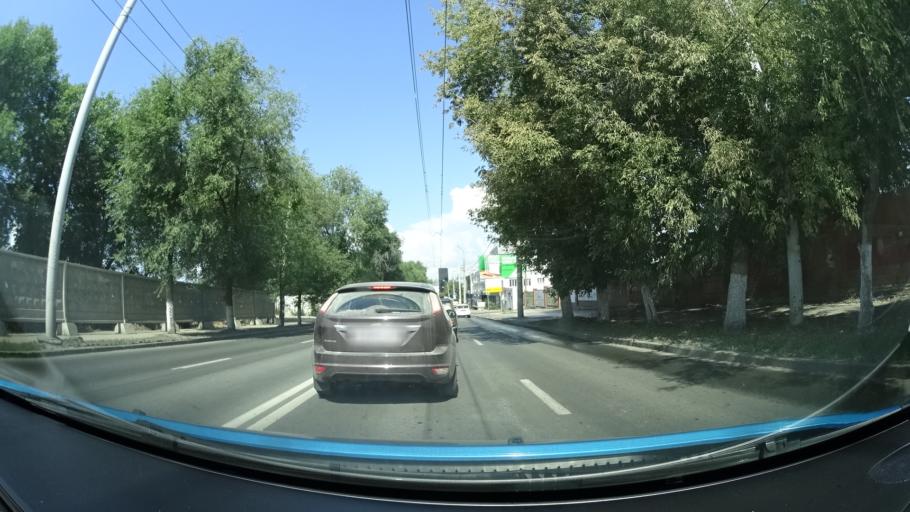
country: RU
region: Samara
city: Samara
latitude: 53.2146
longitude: 50.1517
